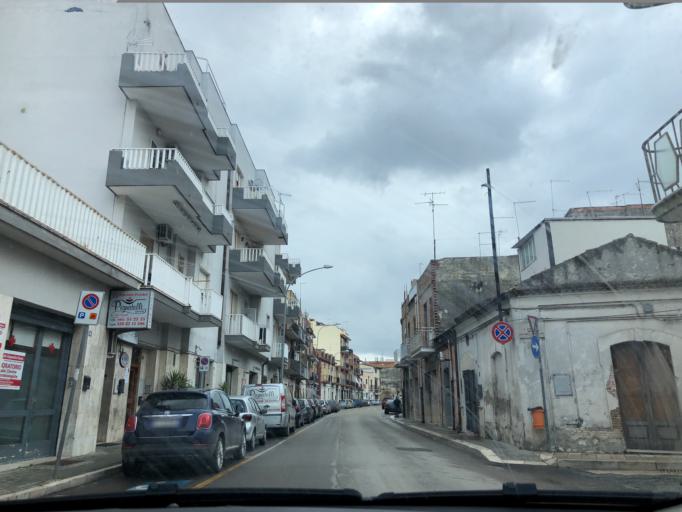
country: IT
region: Apulia
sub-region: Provincia di Foggia
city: Lucera
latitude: 41.5093
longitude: 15.3398
